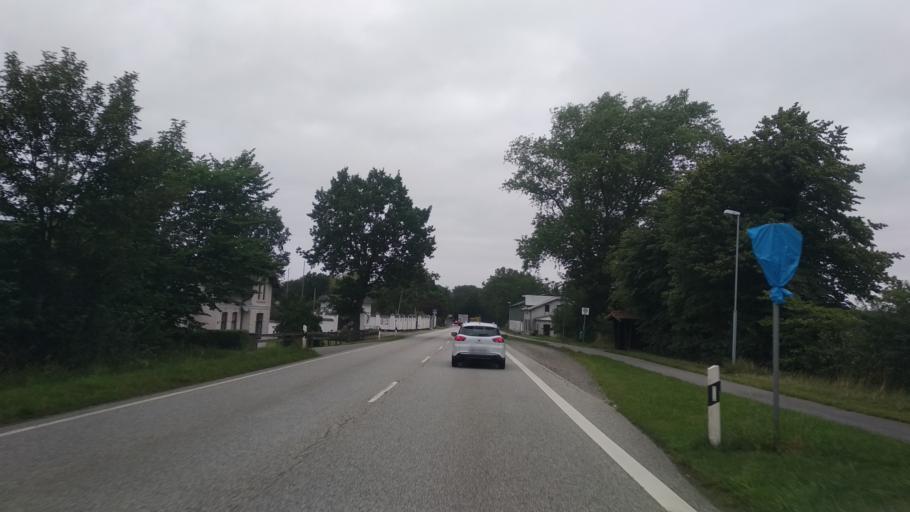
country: DE
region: Schleswig-Holstein
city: Oeversee
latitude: 54.7016
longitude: 9.4362
